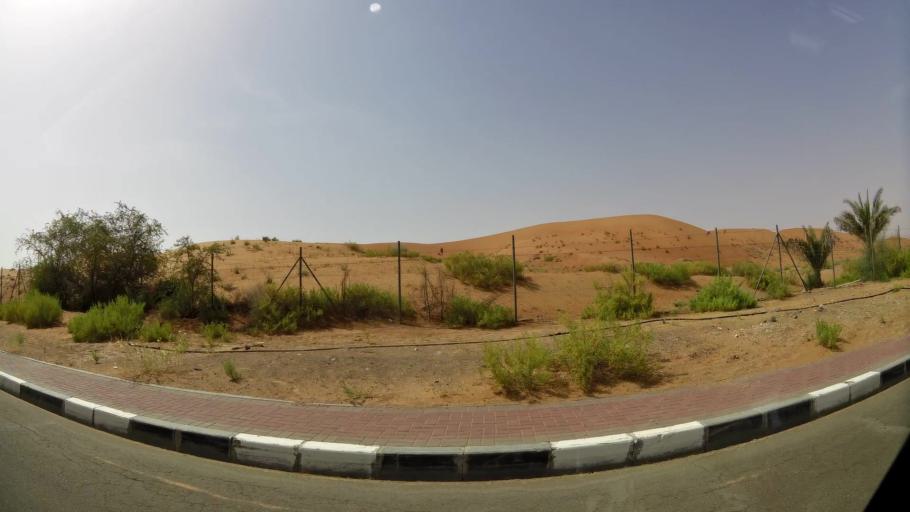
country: AE
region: Abu Dhabi
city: Al Ain
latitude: 24.1558
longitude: 55.6801
